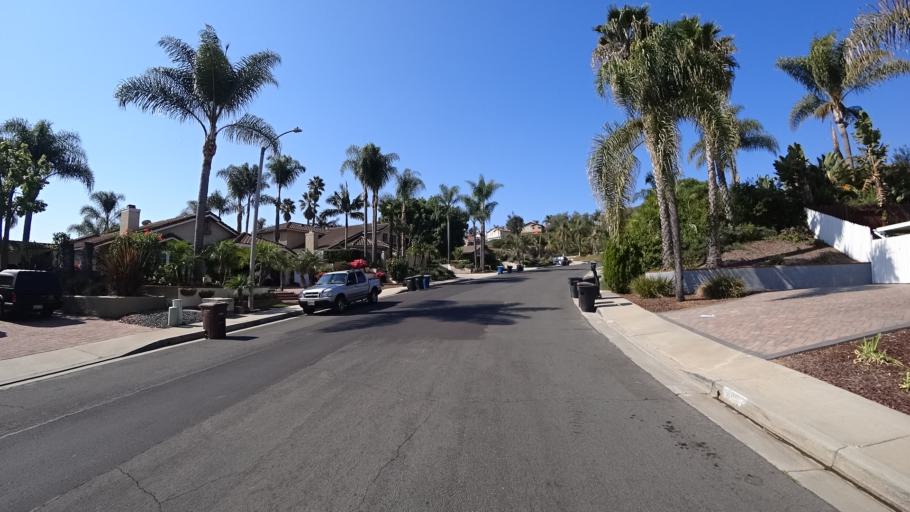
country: US
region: California
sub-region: Orange County
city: San Juan Capistrano
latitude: 33.4711
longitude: -117.6376
